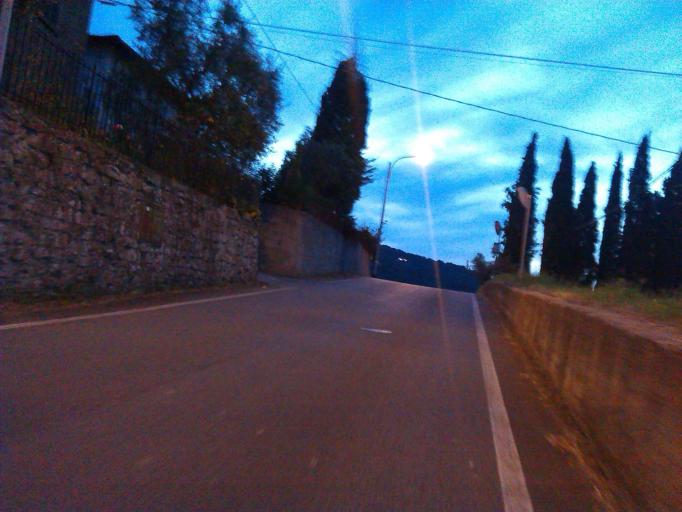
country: IT
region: Tuscany
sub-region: Province of Arezzo
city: Battifolle-Ruscello-Poggiola
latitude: 43.4496
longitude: 11.7946
